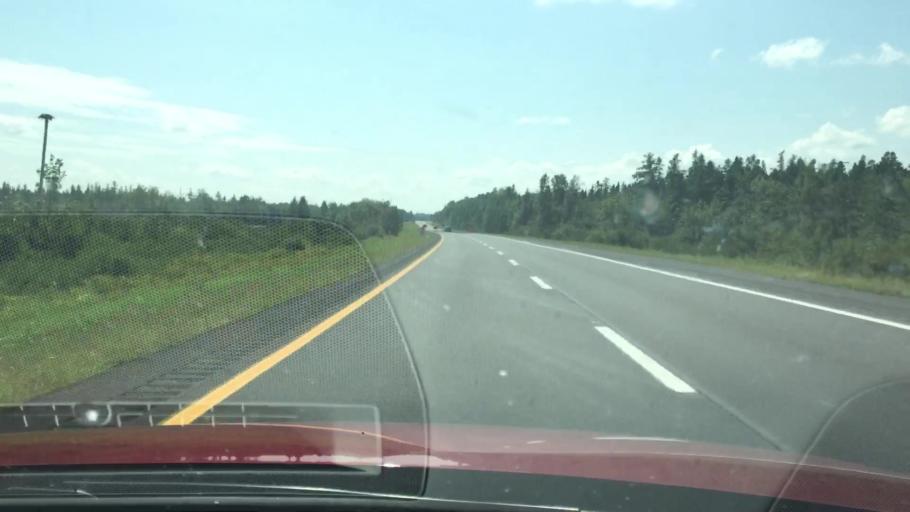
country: US
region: Maine
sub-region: Penobscot County
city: Patten
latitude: 45.8855
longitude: -68.4075
